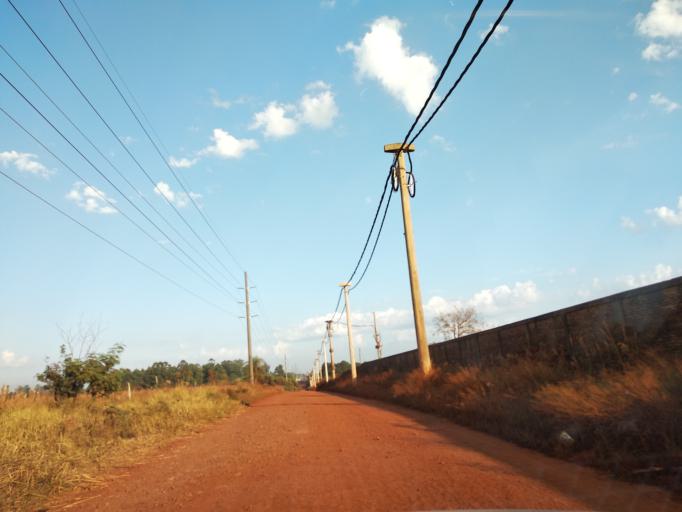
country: AR
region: Misiones
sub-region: Departamento de Capital
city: Posadas
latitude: -27.4440
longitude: -55.9258
